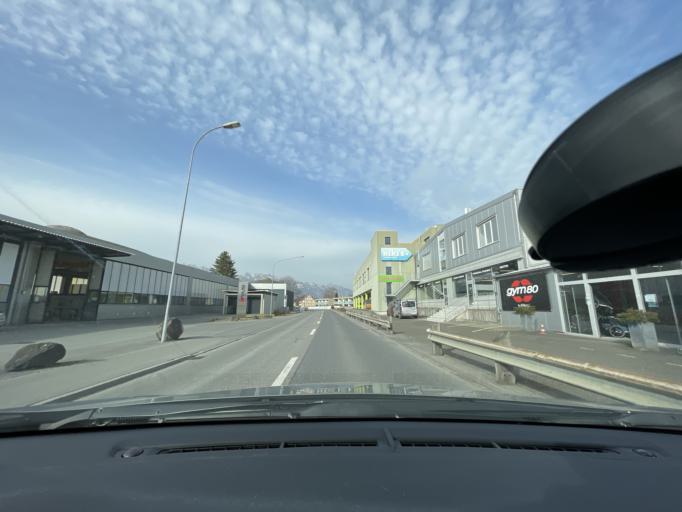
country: CH
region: Saint Gallen
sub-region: Wahlkreis Werdenberg
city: Sevelen
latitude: 47.1425
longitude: 9.4859
